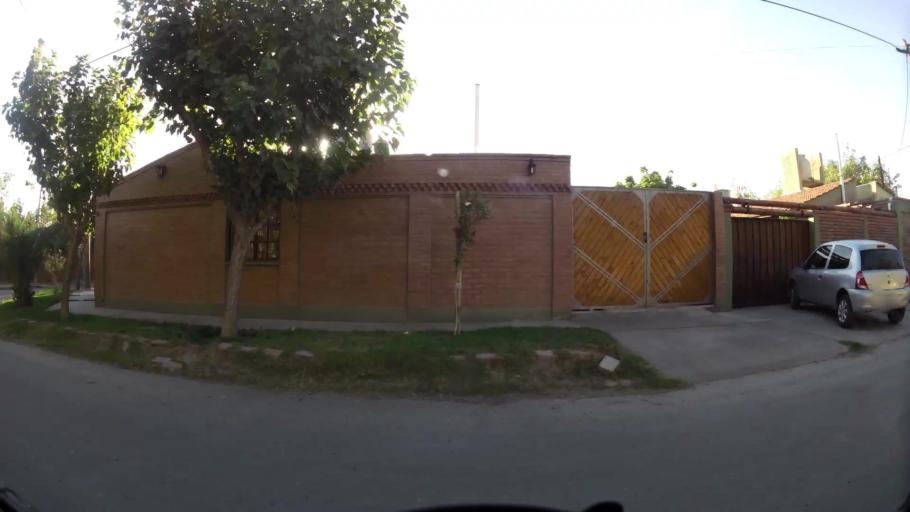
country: AR
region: San Juan
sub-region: Departamento de Santa Lucia
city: Santa Lucia
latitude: -31.5495
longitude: -68.5087
